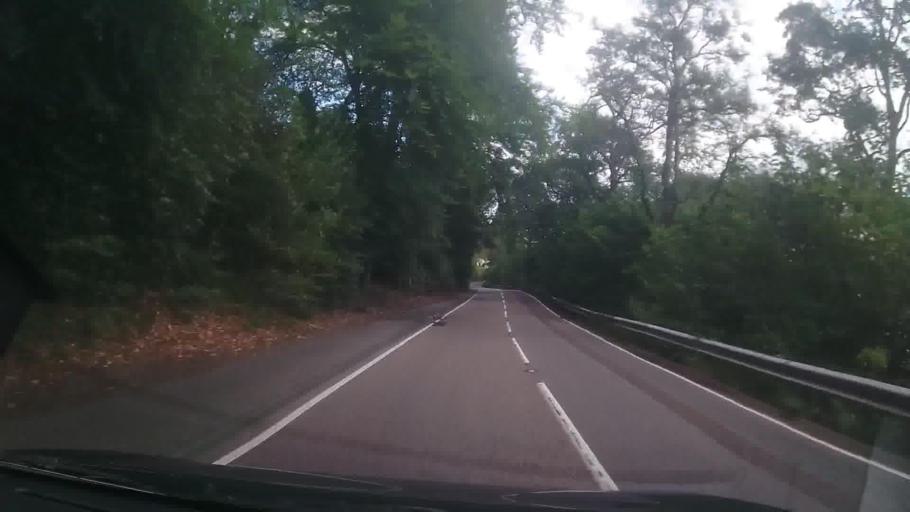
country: GB
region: Scotland
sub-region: Argyll and Bute
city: Garelochhead
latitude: 56.3983
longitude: -5.0511
